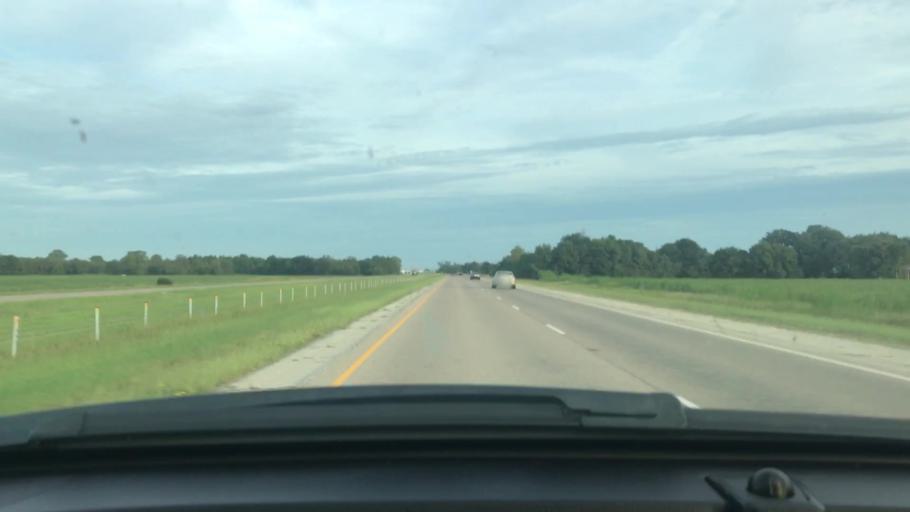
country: US
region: Arkansas
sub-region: Craighead County
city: Bay
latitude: 35.7871
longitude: -90.6044
